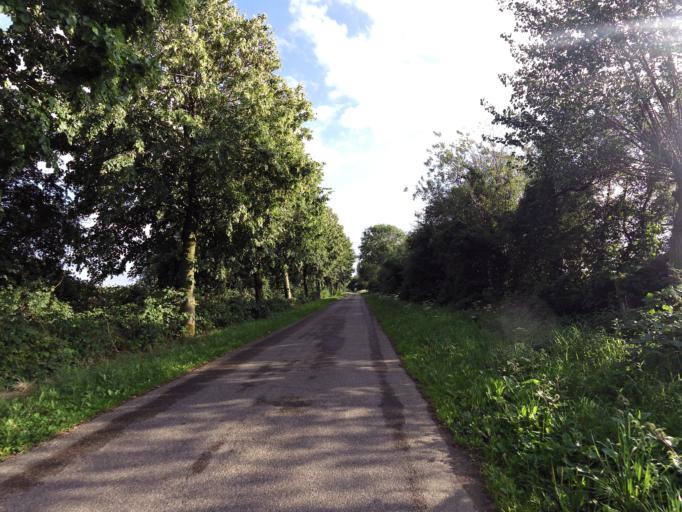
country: NL
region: Gelderland
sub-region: Gemeente Doesburg
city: Doesburg
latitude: 51.9854
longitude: 6.1158
